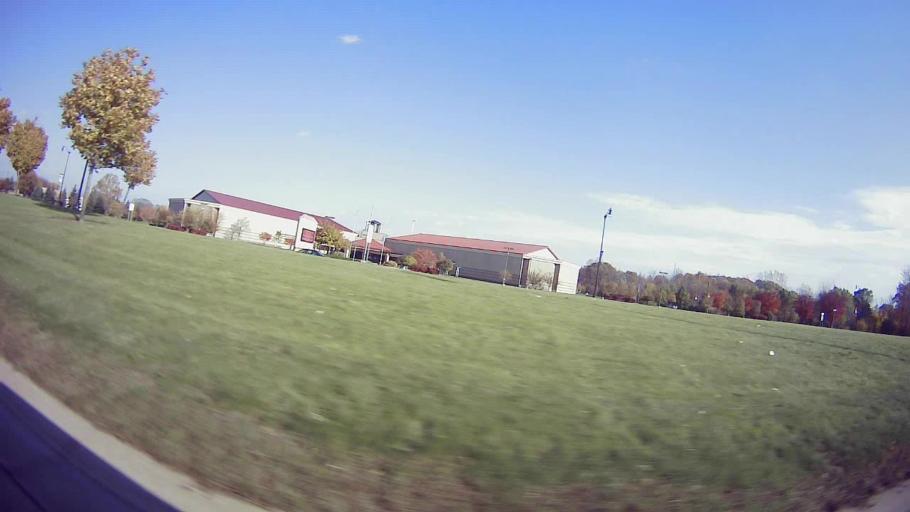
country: US
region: Michigan
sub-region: Wayne County
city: Taylor
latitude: 42.2089
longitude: -83.2688
